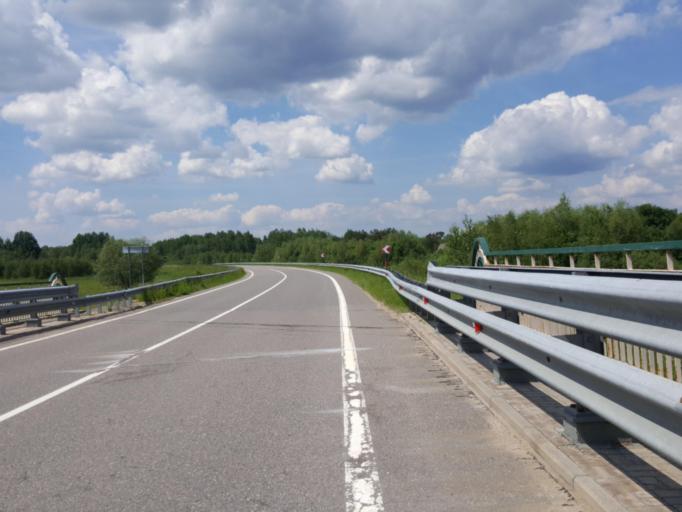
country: BY
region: Brest
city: Kamyanyuki
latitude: 52.5483
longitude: 23.6513
